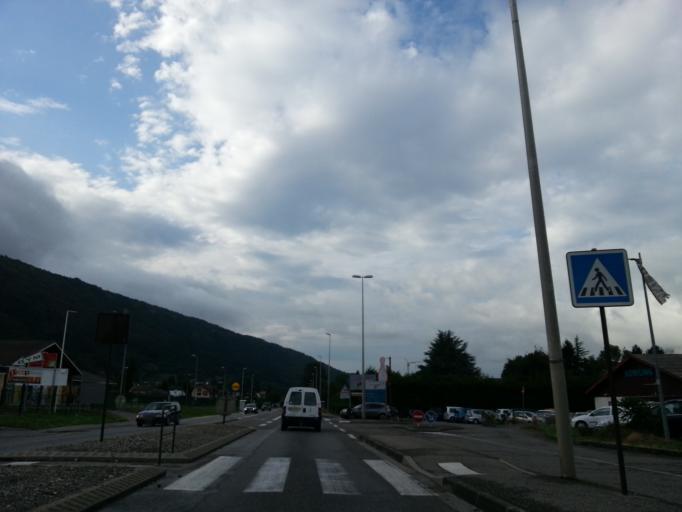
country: FR
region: Rhone-Alpes
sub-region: Departement de la Haute-Savoie
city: Sevrier
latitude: 45.8513
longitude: 6.1451
